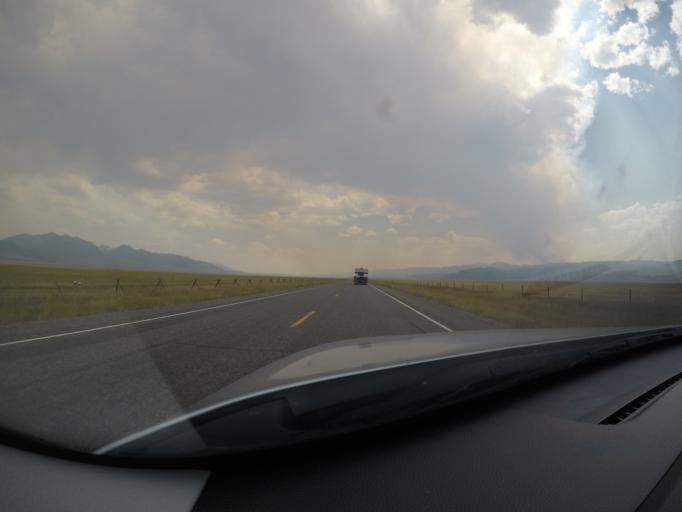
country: US
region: Montana
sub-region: Madison County
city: Virginia City
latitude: 45.1558
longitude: -111.6786
